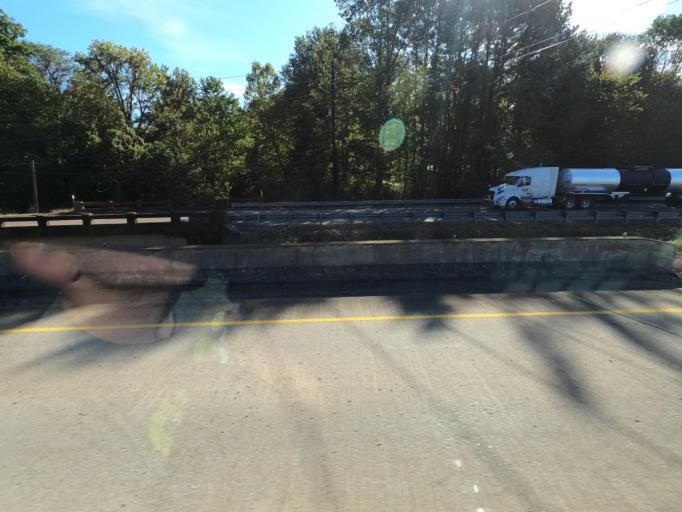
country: US
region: Tennessee
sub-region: Tipton County
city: Brighton
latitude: 35.4968
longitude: -89.7225
